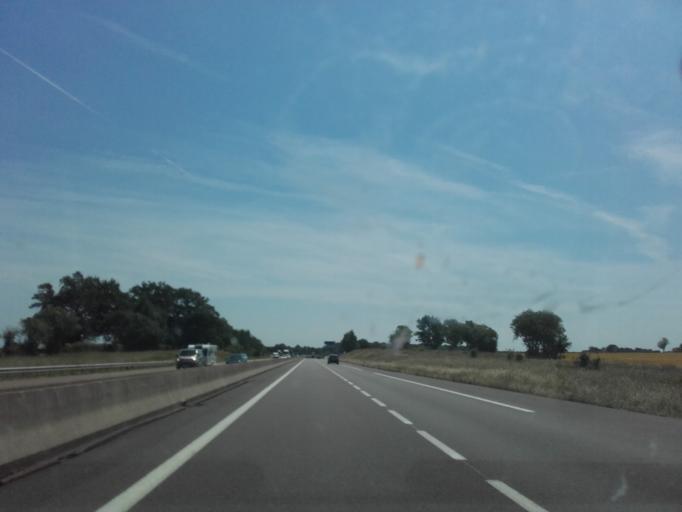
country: FR
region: Bourgogne
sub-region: Departement de la Cote-d'Or
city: Semur-en-Auxois
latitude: 47.4514
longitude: 4.2723
